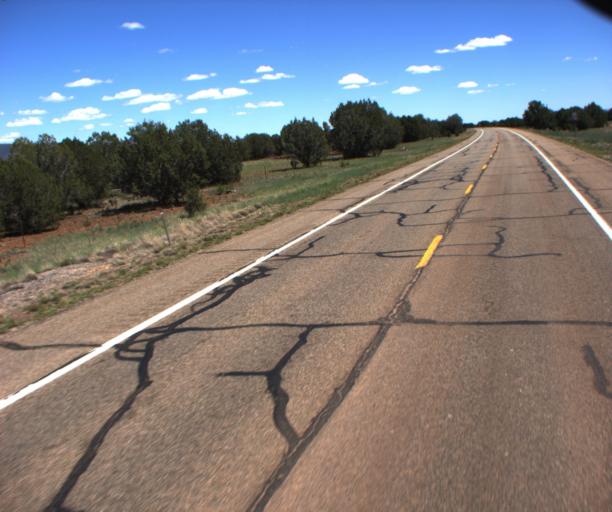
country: US
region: Arizona
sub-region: Yavapai County
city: Paulden
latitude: 35.0972
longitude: -112.4218
